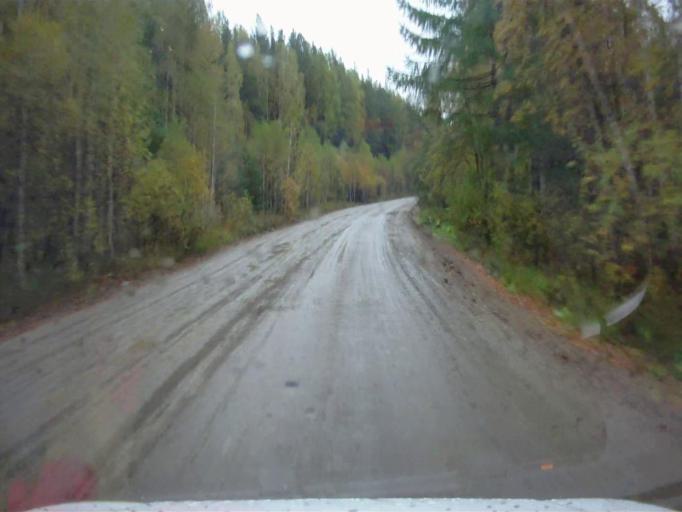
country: RU
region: Chelyabinsk
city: Kyshtym
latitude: 55.7506
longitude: 60.4871
